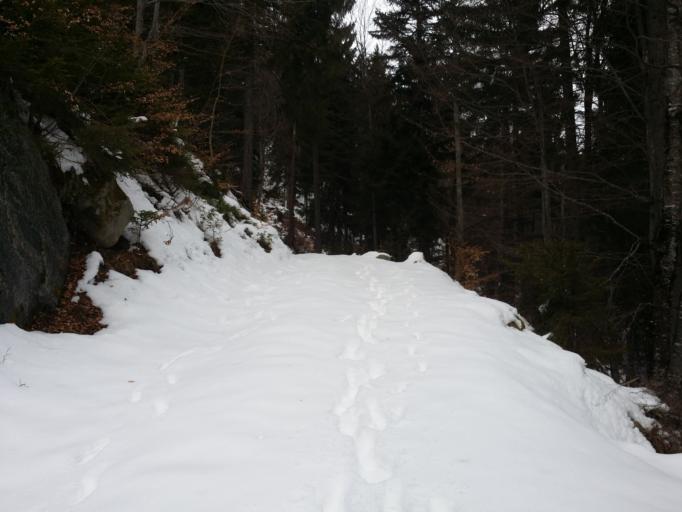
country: IT
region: Piedmont
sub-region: Provincia Verbano-Cusio-Ossola
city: Crodo
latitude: 46.2200
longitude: 8.2917
